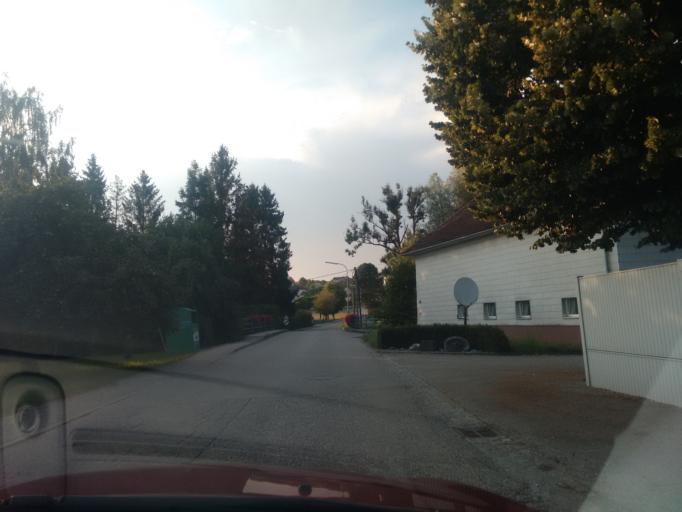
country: AT
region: Upper Austria
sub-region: Politischer Bezirk Grieskirchen
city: Bad Schallerbach
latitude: 48.1857
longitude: 13.8987
